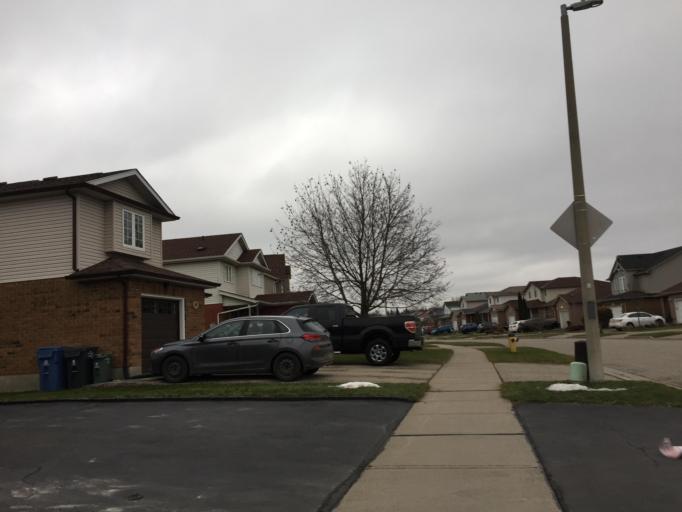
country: CA
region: Ontario
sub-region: Wellington County
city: Guelph
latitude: 43.5268
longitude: -80.2786
